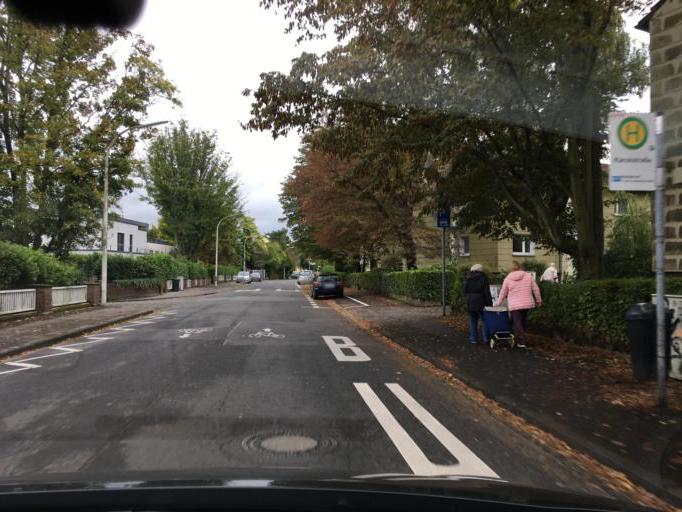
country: DE
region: North Rhine-Westphalia
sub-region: Regierungsbezirk Koln
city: Konigswinter
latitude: 50.7021
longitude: 7.1627
